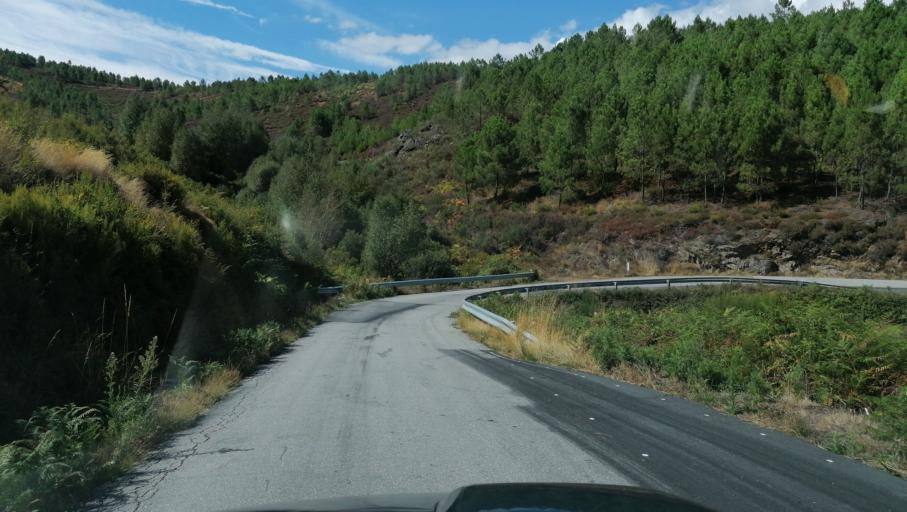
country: PT
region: Vila Real
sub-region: Vila Pouca de Aguiar
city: Vila Pouca de Aguiar
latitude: 41.5537
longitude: -7.7121
